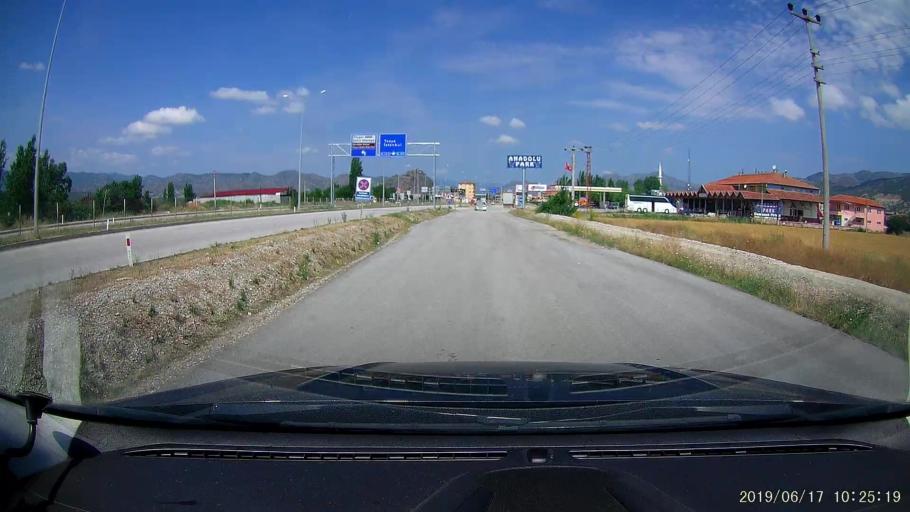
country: TR
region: Corum
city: Osmancik
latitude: 40.9710
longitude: 34.8270
